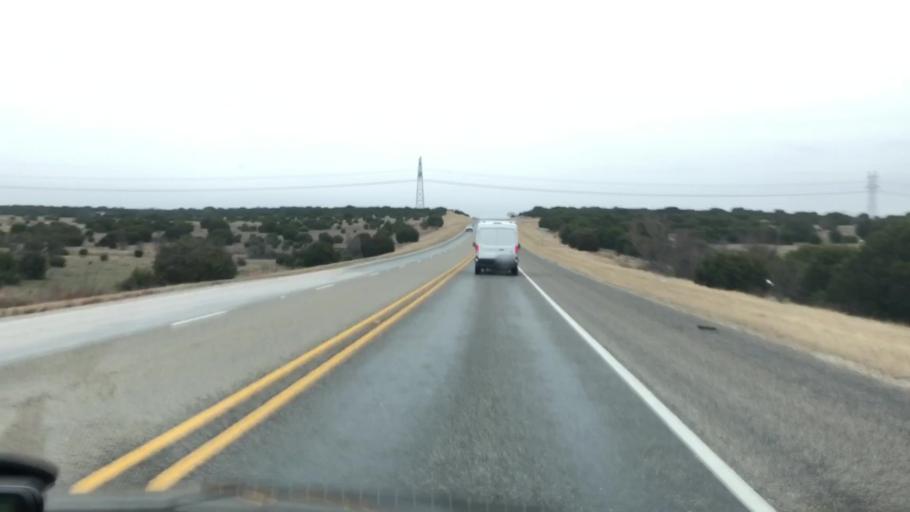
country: US
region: Texas
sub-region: Lampasas County
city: Lampasas
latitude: 31.1390
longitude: -98.1853
